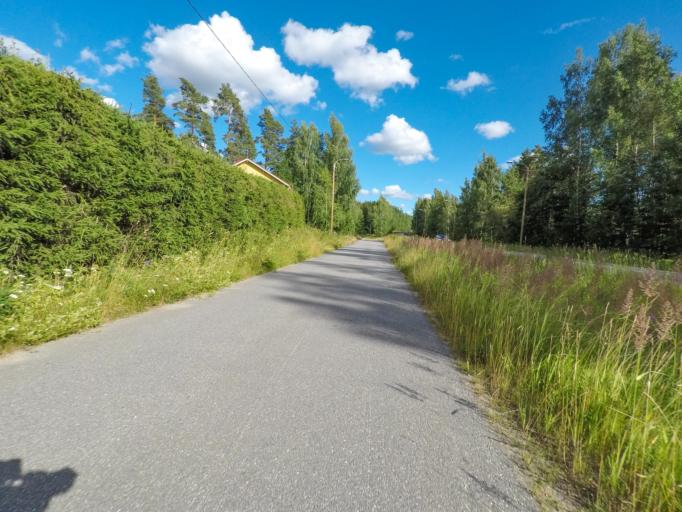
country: FI
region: South Karelia
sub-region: Lappeenranta
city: Taipalsaari
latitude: 61.1062
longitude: 28.1182
